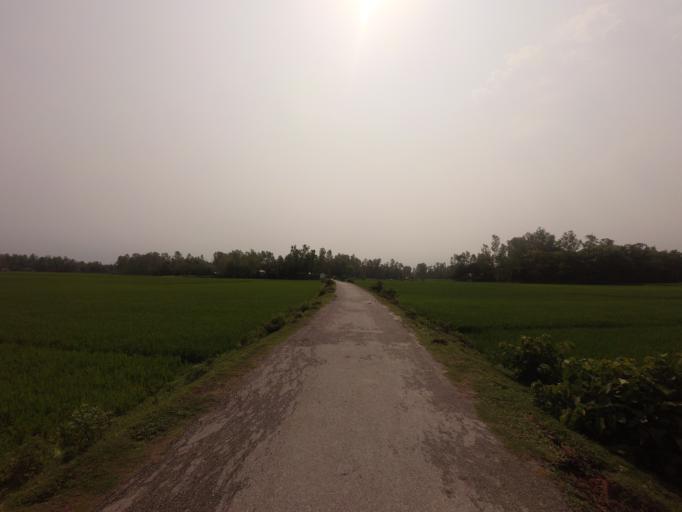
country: BD
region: Rajshahi
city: Sirajganj
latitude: 24.3216
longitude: 89.6767
